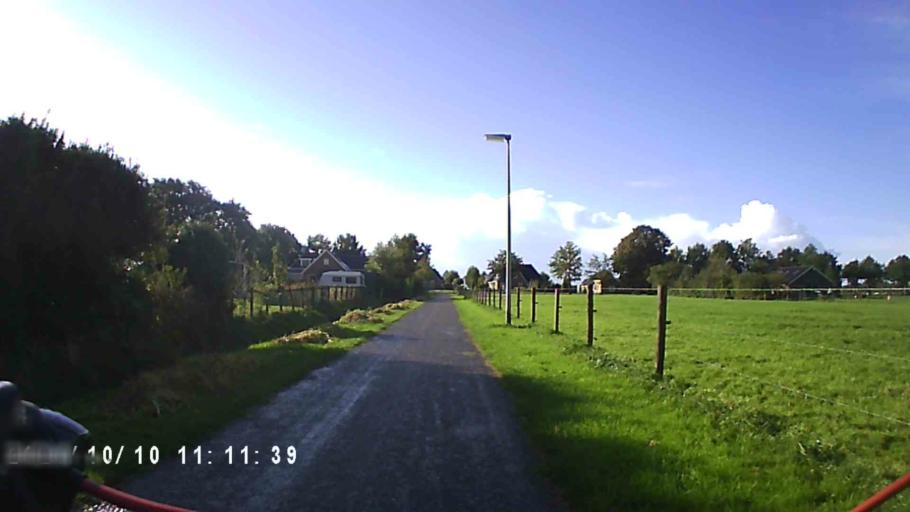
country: NL
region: Friesland
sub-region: Gemeente Smallingerland
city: Drachtstercompagnie
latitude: 53.1128
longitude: 6.2053
